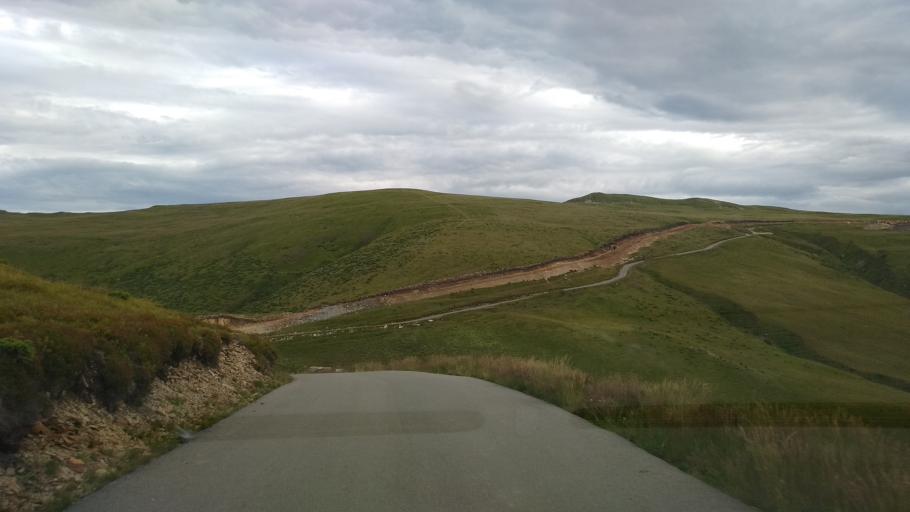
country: RO
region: Hunedoara
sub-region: Municipiul  Vulcan
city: Jiu-Paroseni
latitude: 45.3104
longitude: 23.3087
